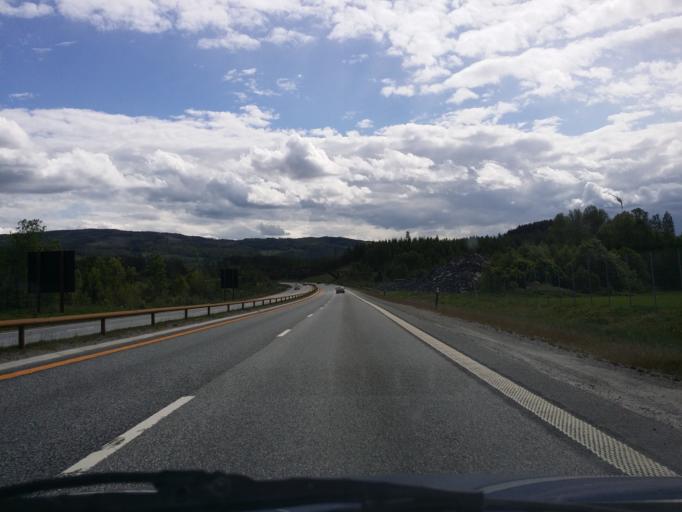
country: NO
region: Hedmark
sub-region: Stange
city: Stange
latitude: 60.6245
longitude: 11.2993
